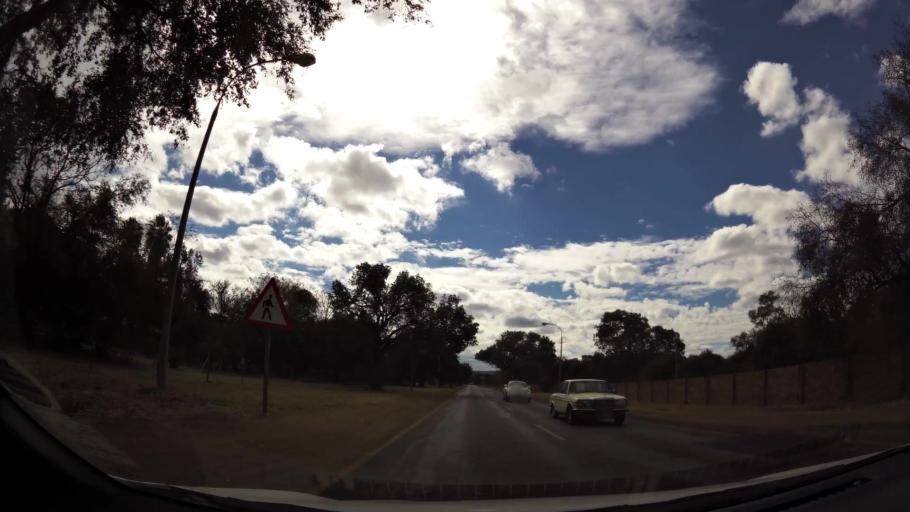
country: ZA
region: Limpopo
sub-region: Waterberg District Municipality
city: Warmbaths
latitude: -24.8918
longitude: 28.2831
